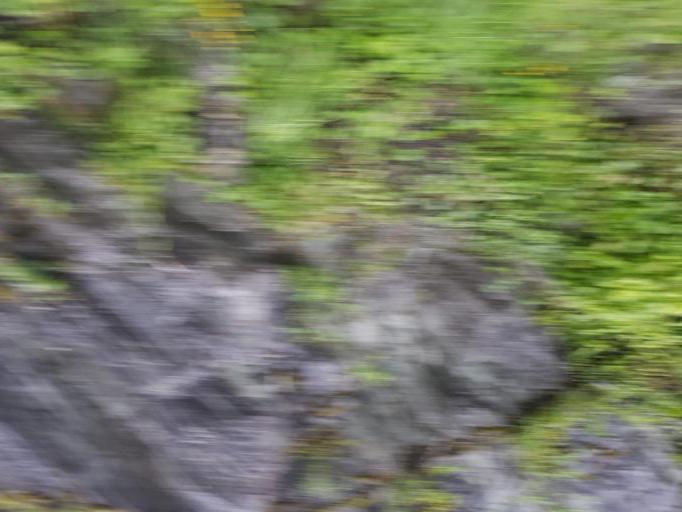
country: NO
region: Sor-Trondelag
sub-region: Selbu
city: Mebonden
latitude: 63.3207
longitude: 11.0846
